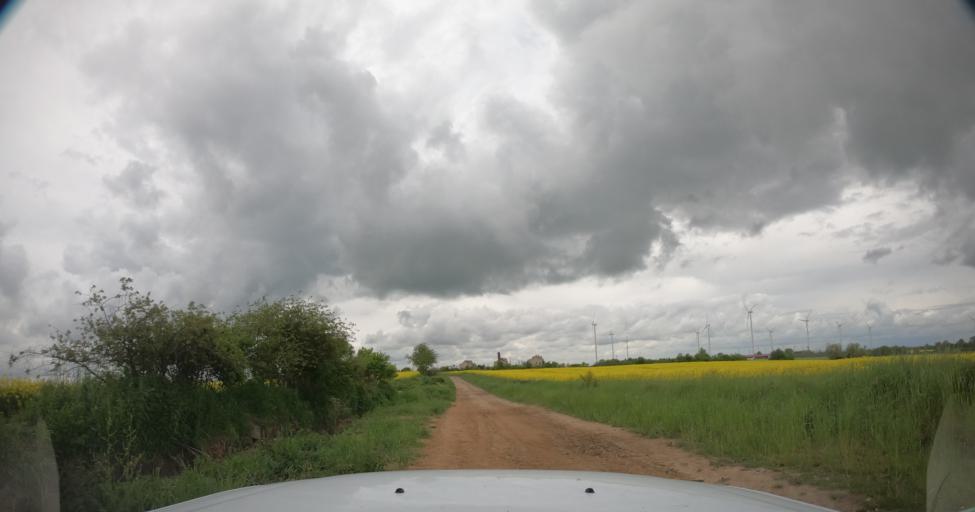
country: PL
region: West Pomeranian Voivodeship
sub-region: Powiat pyrzycki
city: Kozielice
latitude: 53.0937
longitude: 14.8115
